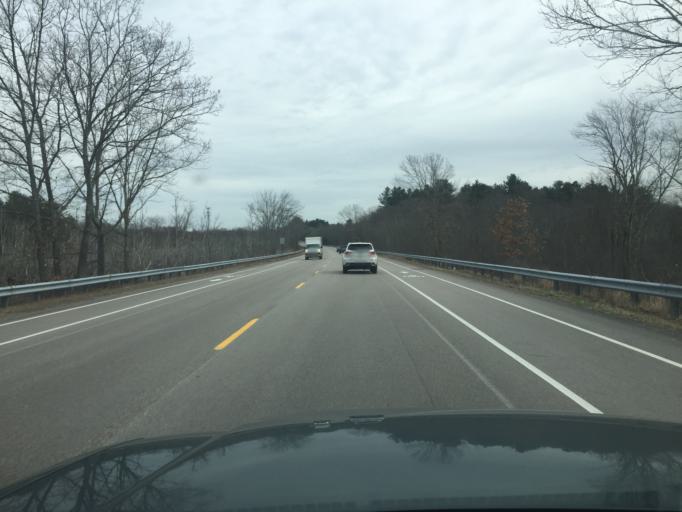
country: US
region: Massachusetts
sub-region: Norfolk County
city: Medfield
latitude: 42.2003
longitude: -71.3349
